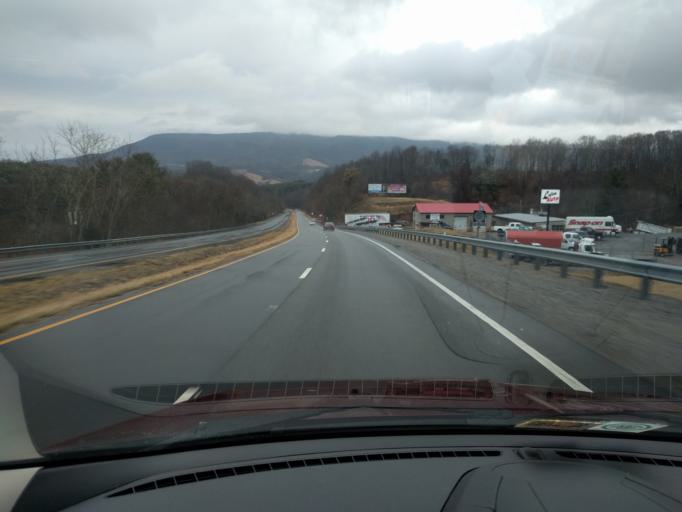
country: US
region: Virginia
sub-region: Montgomery County
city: Prices Fork
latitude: 37.2979
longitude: -80.5025
